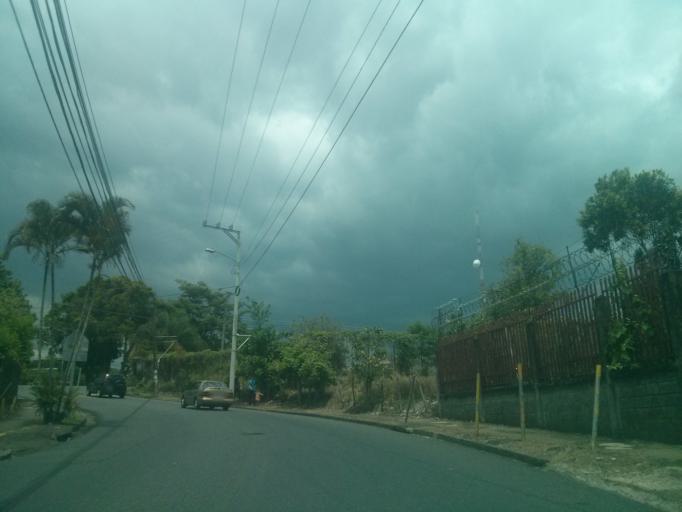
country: CR
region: San Jose
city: San Pedro
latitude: 9.9252
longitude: -84.0665
